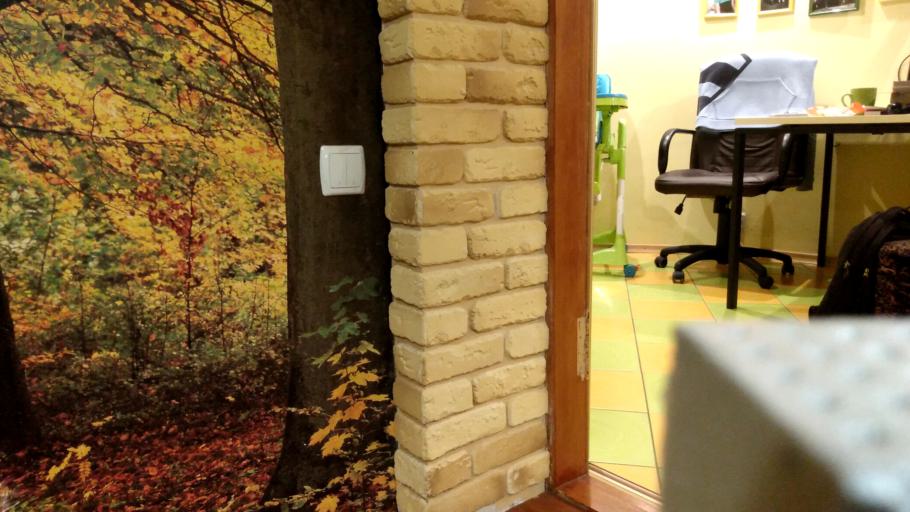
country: RU
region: Republic of Karelia
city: Pudozh
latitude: 61.7371
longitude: 37.6945
